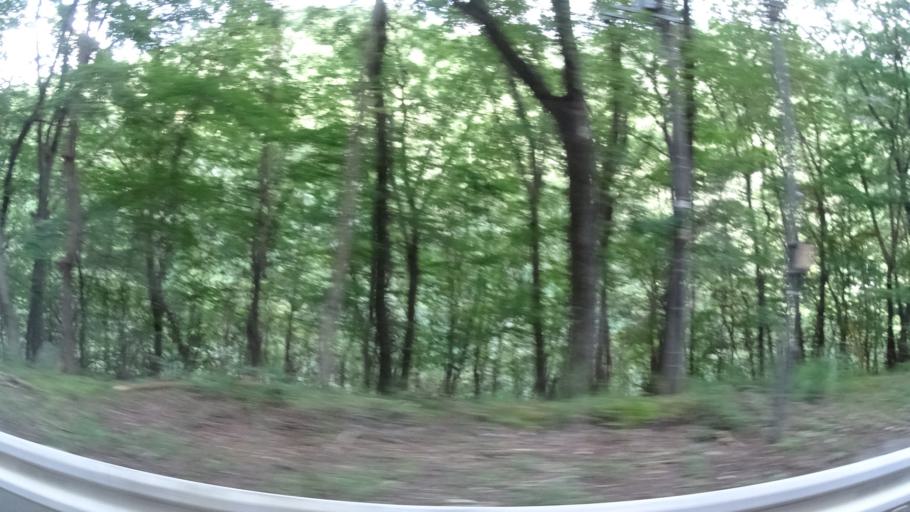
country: JP
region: Tochigi
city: Nikko
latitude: 36.6505
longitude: 139.4540
